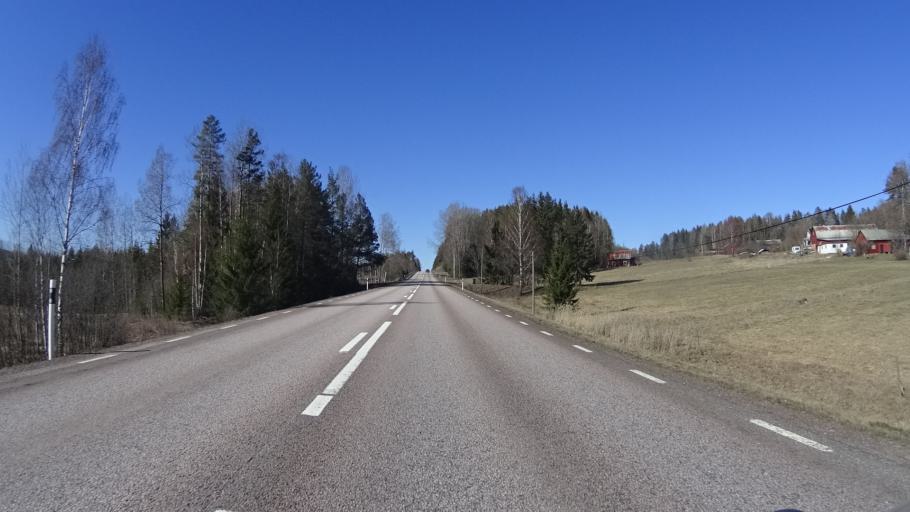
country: SE
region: Vaermland
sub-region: Karlstads Kommun
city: Edsvalla
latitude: 59.5816
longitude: 13.0162
